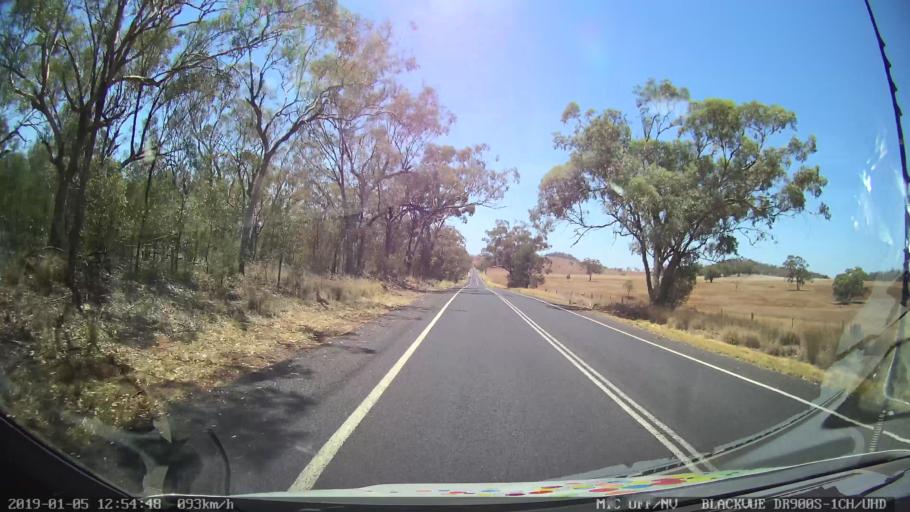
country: AU
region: New South Wales
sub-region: Warrumbungle Shire
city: Coonabarabran
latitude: -31.1184
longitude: 149.6948
